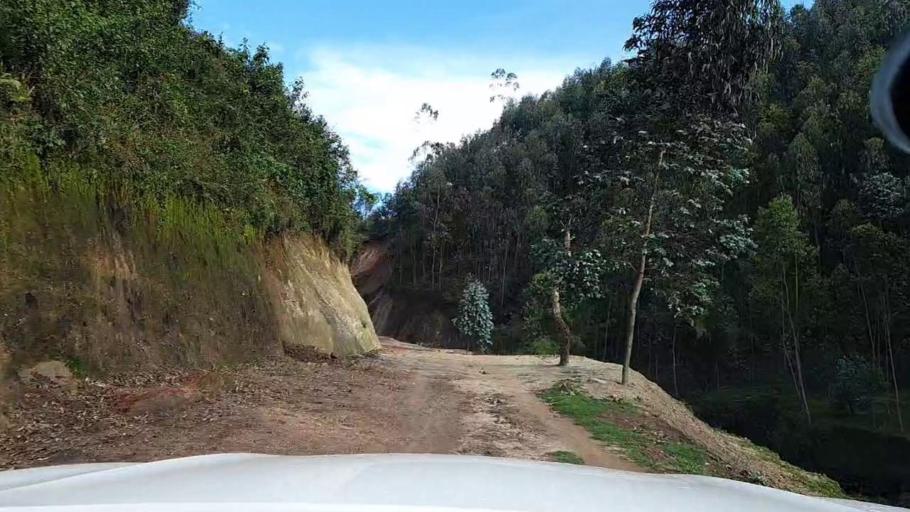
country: BI
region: Kayanza
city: Kayanza
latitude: -2.7810
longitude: 29.4523
